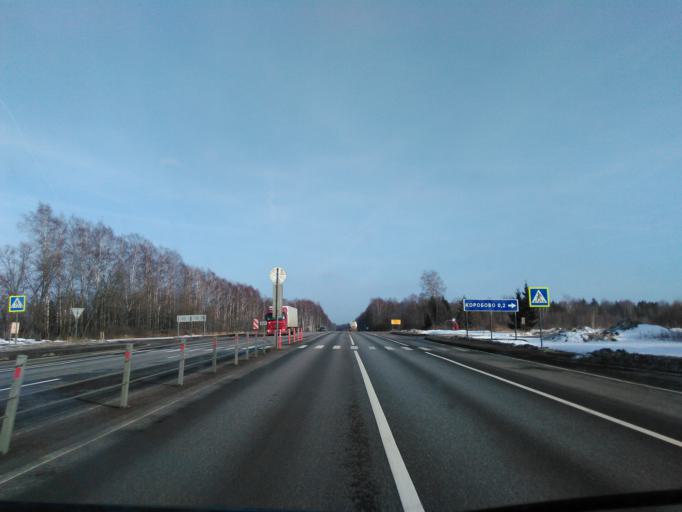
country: RU
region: Smolensk
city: Vyaz'ma
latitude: 55.1884
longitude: 34.0359
